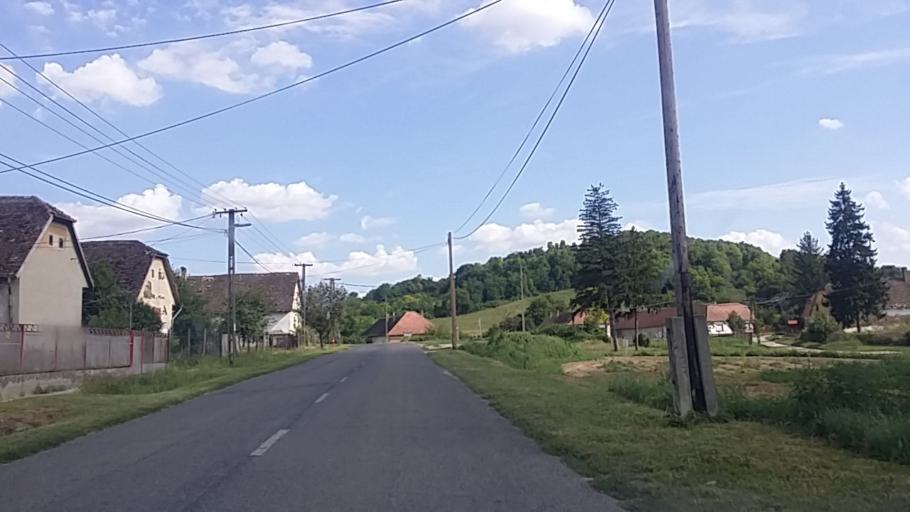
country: HU
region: Tolna
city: Gyonk
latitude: 46.5224
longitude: 18.5221
